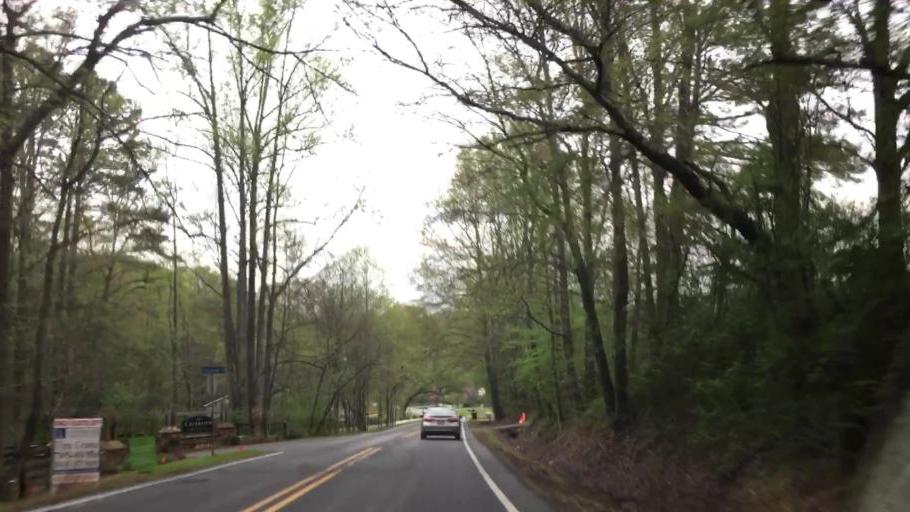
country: US
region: Georgia
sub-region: Cherokee County
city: Canton
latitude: 34.2191
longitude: -84.4034
